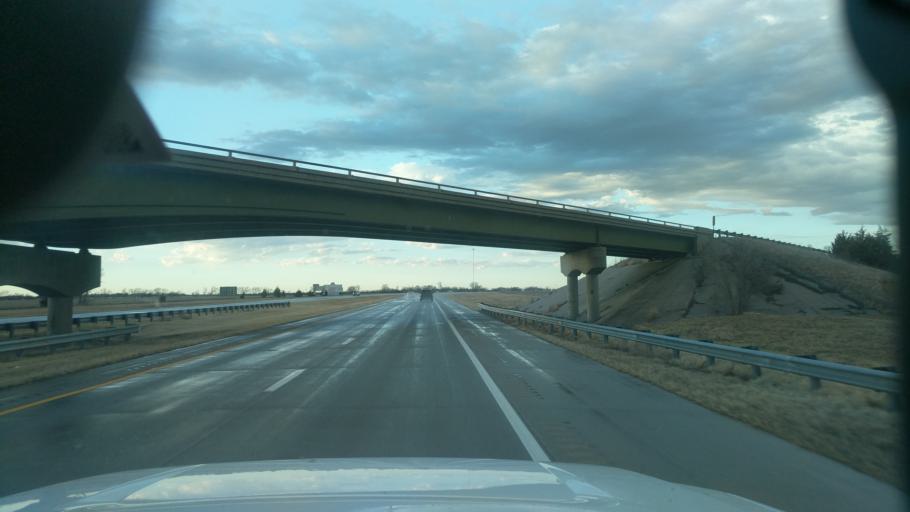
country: US
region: Kansas
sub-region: Harvey County
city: Hesston
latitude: 38.1525
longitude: -97.4269
